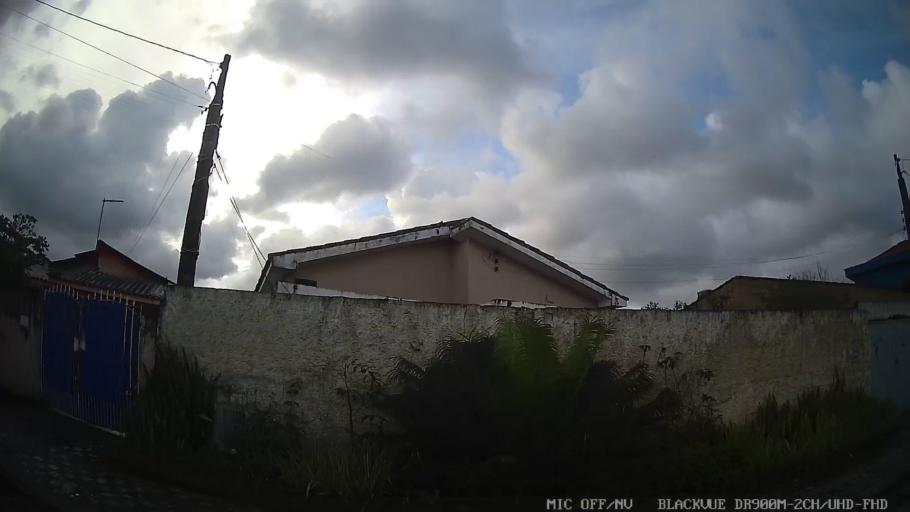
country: BR
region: Sao Paulo
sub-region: Mongagua
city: Mongagua
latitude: -24.1183
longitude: -46.6748
